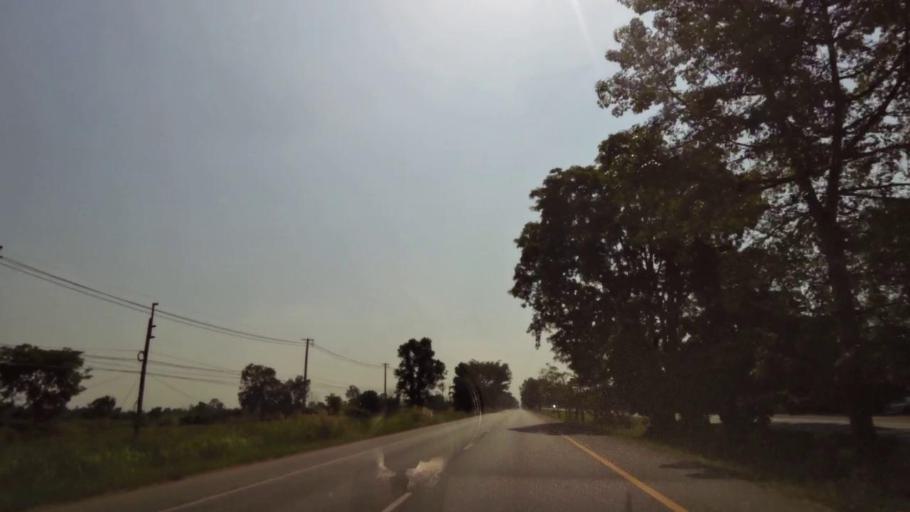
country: TH
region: Phichit
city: Bueng Na Rang
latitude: 16.2901
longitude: 100.1281
